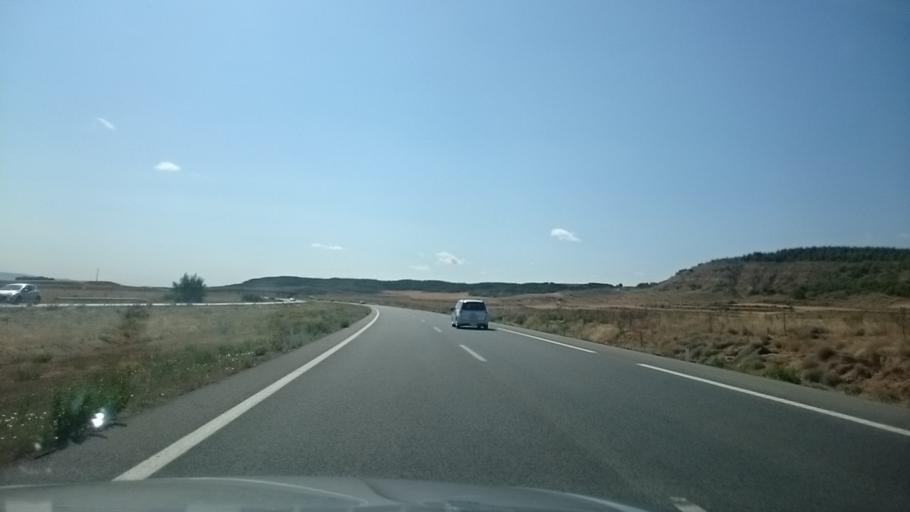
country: ES
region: Navarre
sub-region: Provincia de Navarra
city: Ribaforada
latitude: 41.9428
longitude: -1.5262
